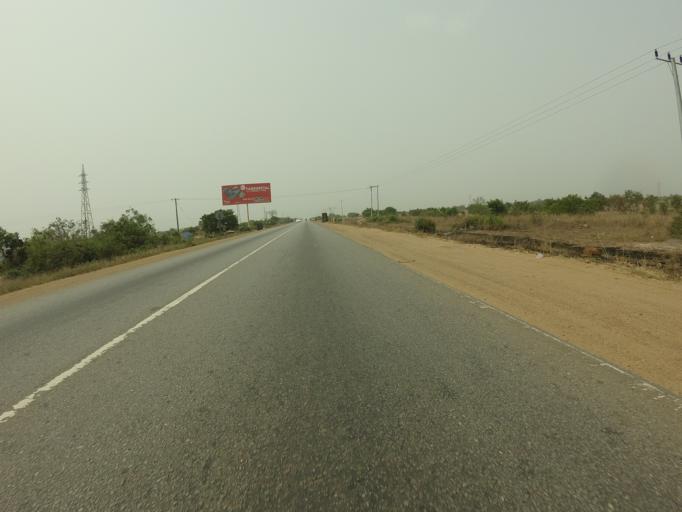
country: GH
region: Greater Accra
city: Tema
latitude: 5.8255
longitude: 0.1960
